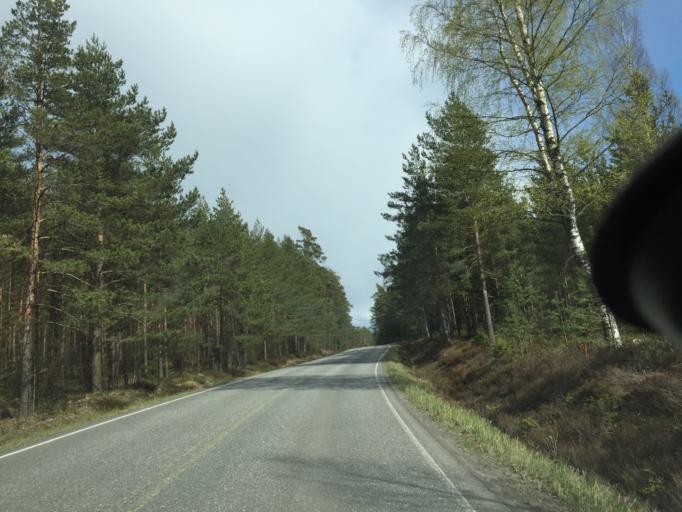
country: FI
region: Uusimaa
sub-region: Raaseporin
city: Hanko
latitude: 59.9730
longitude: 22.9945
